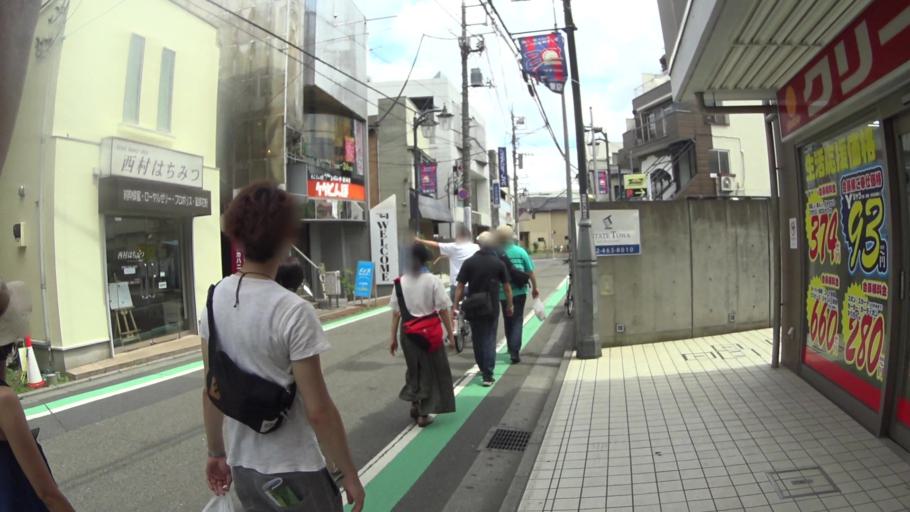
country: JP
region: Tokyo
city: Chofugaoka
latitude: 35.6556
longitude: 139.5672
